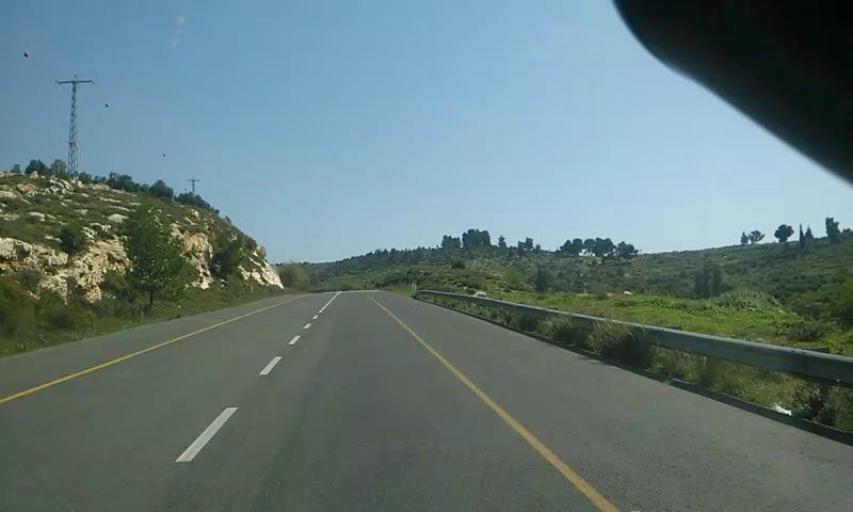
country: PS
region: West Bank
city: Idhna
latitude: 31.5651
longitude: 34.9938
